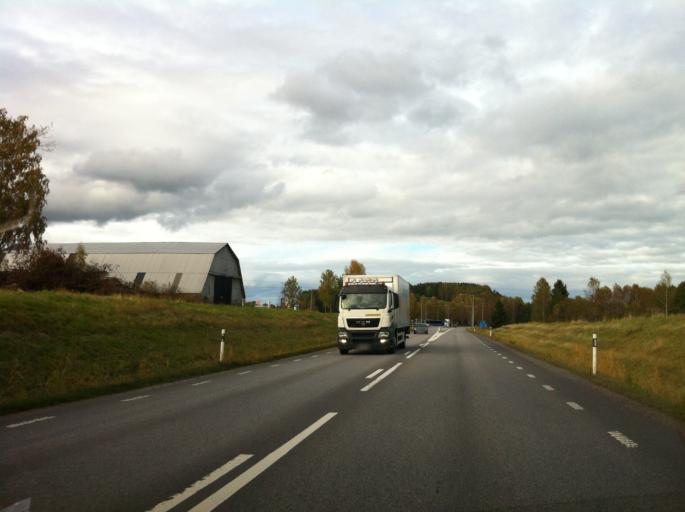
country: SE
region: OErebro
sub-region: Askersunds Kommun
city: Askersund
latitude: 58.8839
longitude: 14.8986
